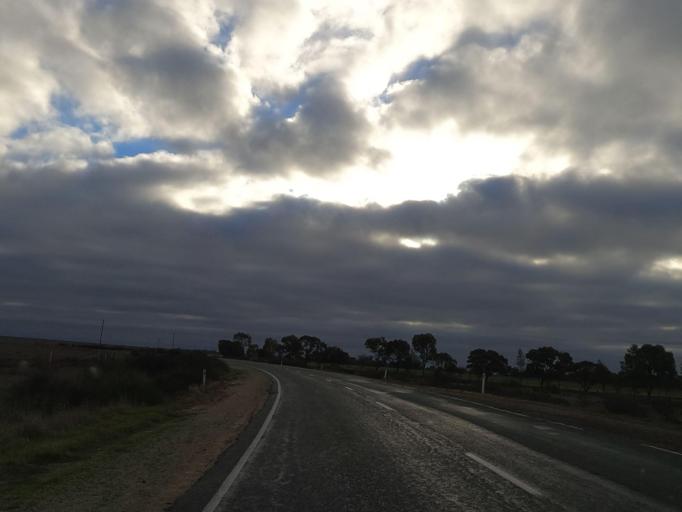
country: AU
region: Victoria
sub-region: Swan Hill
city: Swan Hill
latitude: -35.6511
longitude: 143.8439
